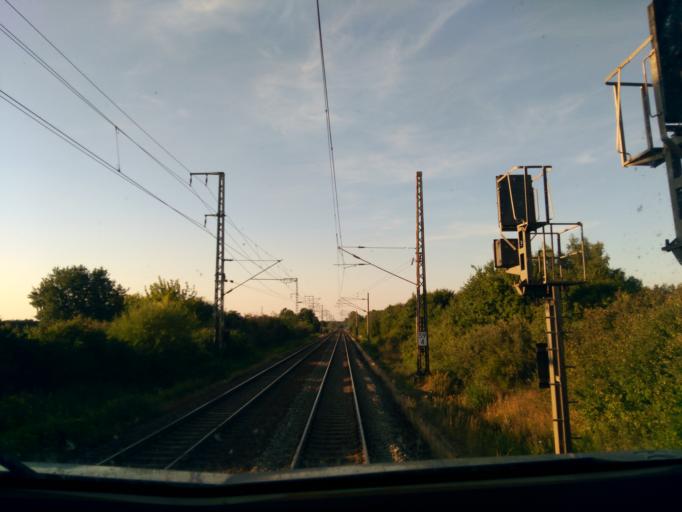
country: DE
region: Mecklenburg-Vorpommern
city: Klein Rogahn
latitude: 53.5763
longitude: 11.3779
